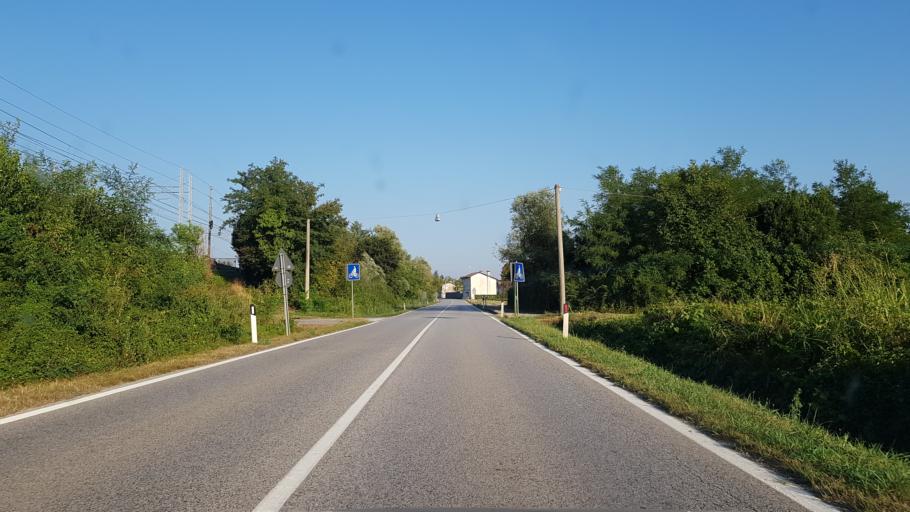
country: IT
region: Friuli Venezia Giulia
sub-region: Provincia di Gorizia
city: Cormons
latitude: 45.9486
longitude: 13.4787
